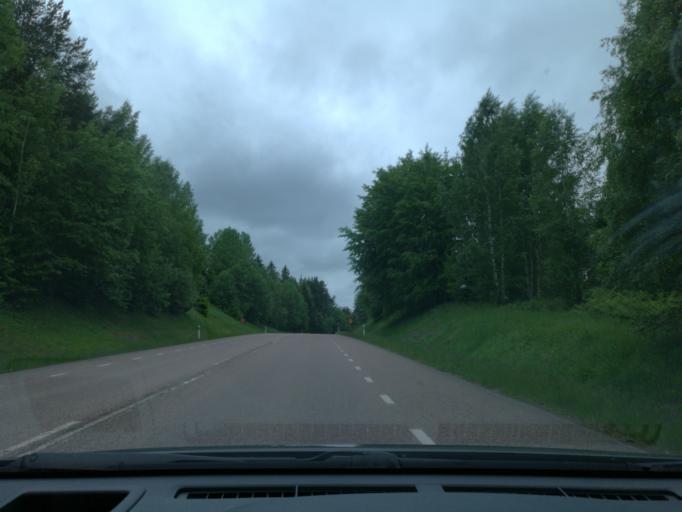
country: SE
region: Dalarna
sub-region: Smedjebackens Kommun
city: Smedjebacken
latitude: 60.1396
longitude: 15.3074
